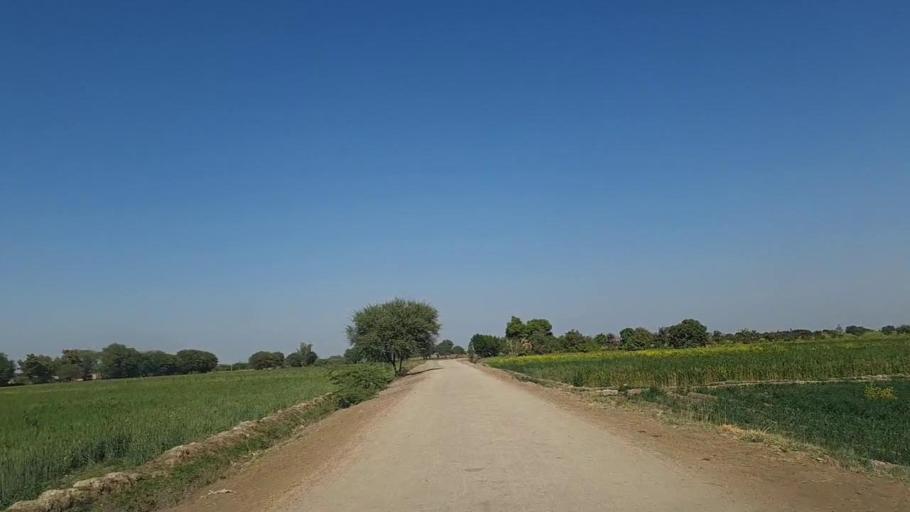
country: PK
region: Sindh
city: Naukot
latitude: 25.0042
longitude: 69.3370
